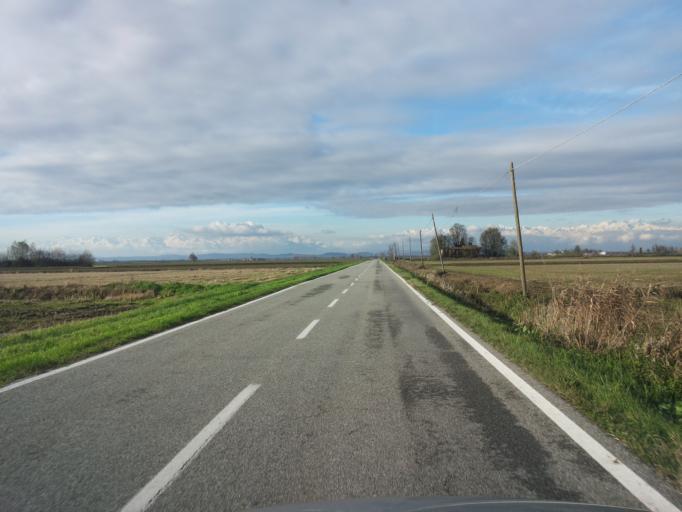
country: IT
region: Piedmont
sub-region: Provincia di Vercelli
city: Crova
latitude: 45.2986
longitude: 8.2173
